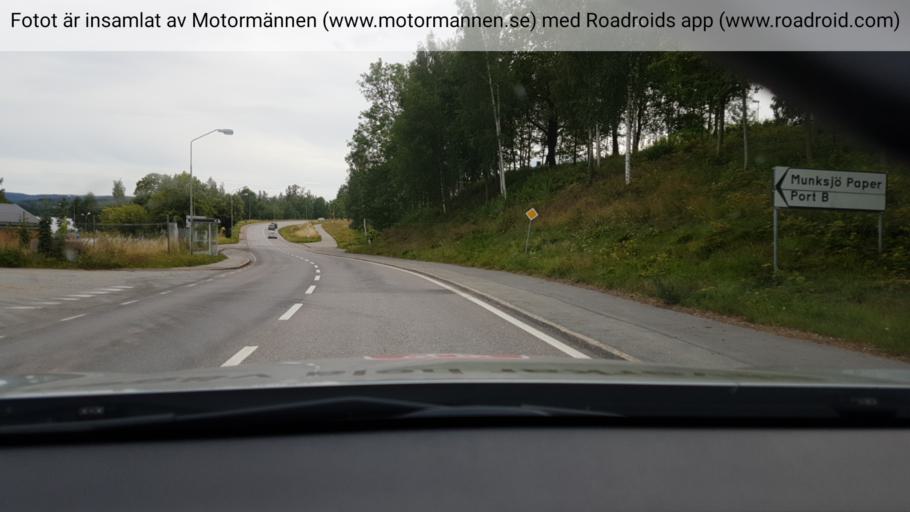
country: SE
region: Vaestra Goetaland
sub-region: Bengtsfors Kommun
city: Billingsfors
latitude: 58.9883
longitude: 12.2528
